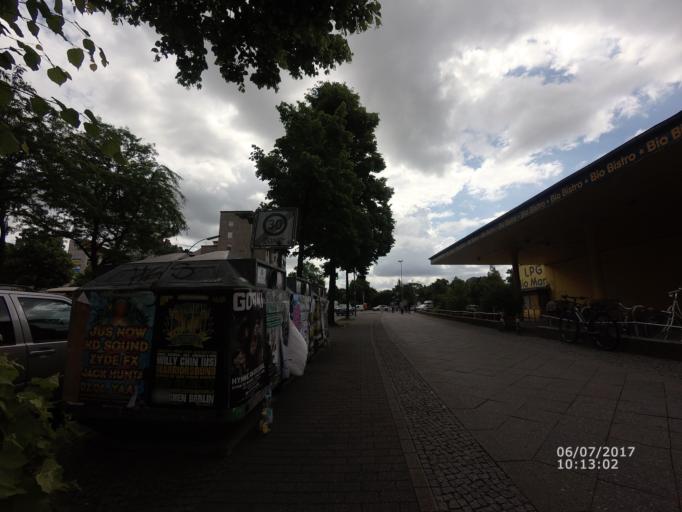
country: DE
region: Berlin
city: Bezirk Kreuzberg
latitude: 52.4961
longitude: 13.3886
